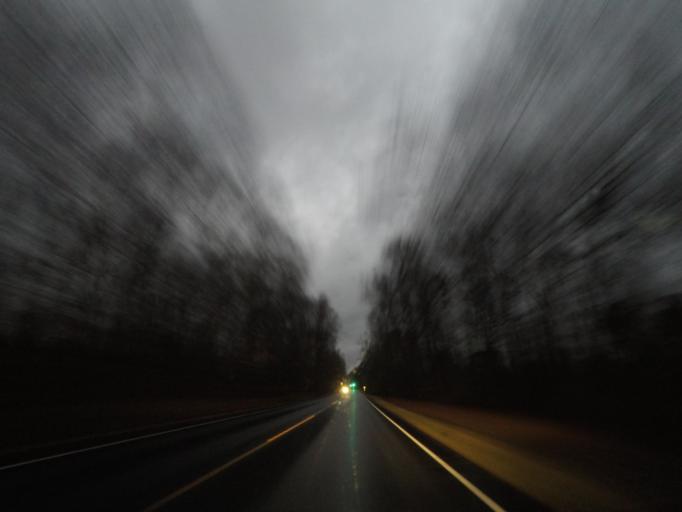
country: US
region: North Carolina
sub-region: Orange County
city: Hillsborough
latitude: 36.0664
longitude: -79.0601
